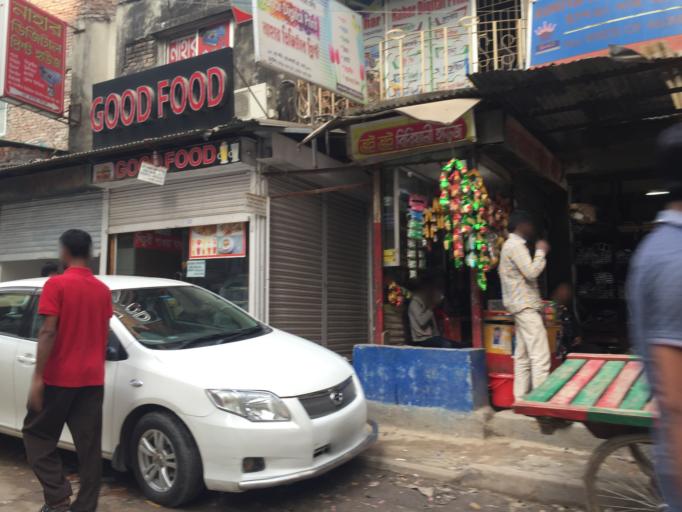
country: BD
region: Dhaka
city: Paltan
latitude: 23.7322
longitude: 90.4135
